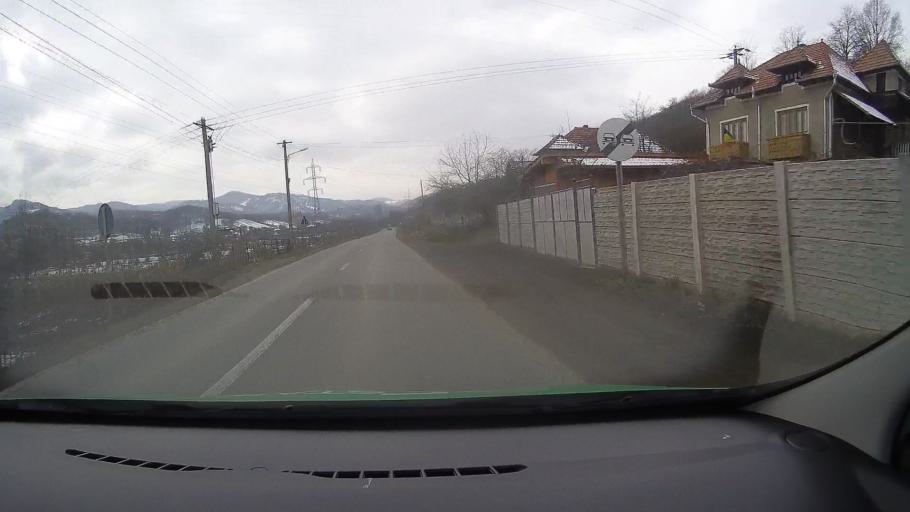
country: RO
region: Alba
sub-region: Oras Zlatna
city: Fenes
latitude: 46.0970
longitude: 23.2994
